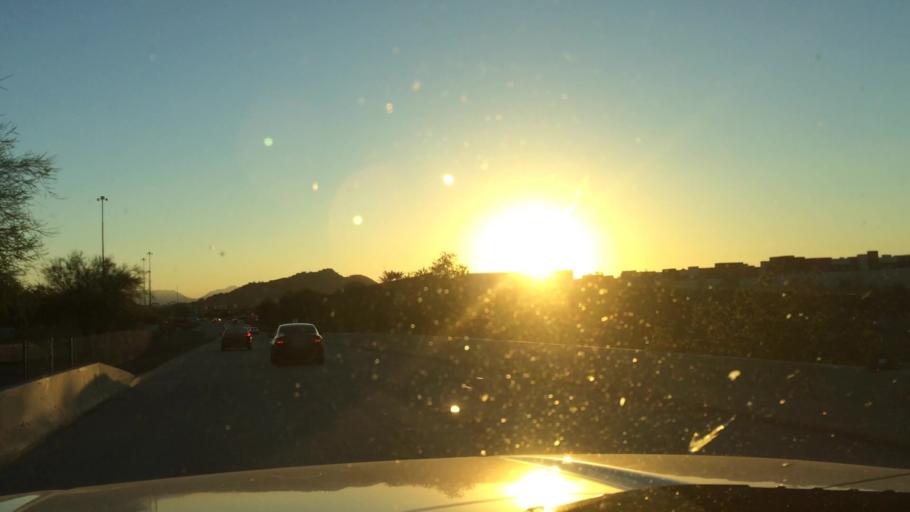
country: US
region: Arizona
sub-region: Maricopa County
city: Glendale
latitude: 33.6673
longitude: -112.0705
